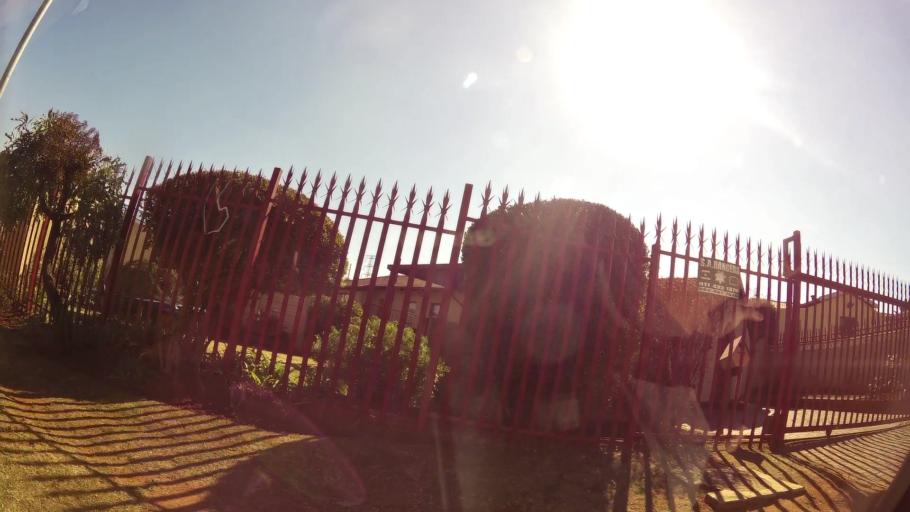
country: ZA
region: Gauteng
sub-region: City of Johannesburg Metropolitan Municipality
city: Johannesburg
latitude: -26.2643
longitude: 27.9909
